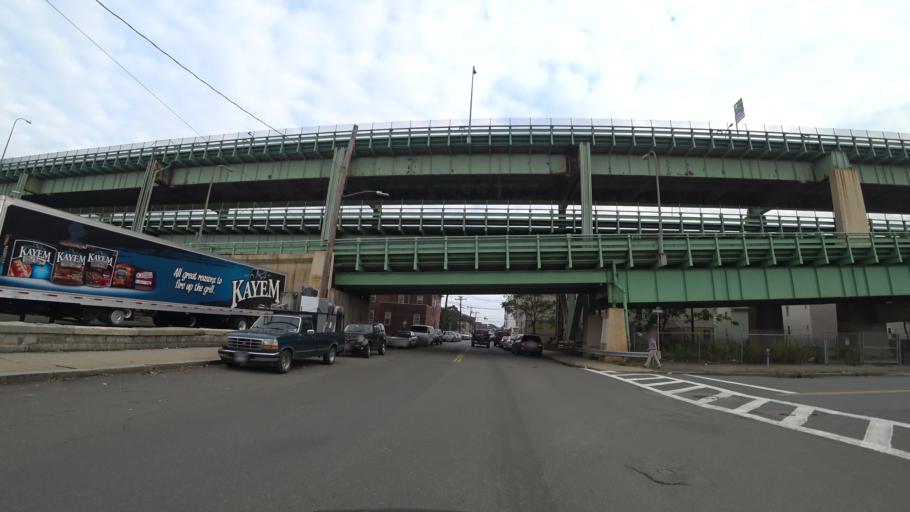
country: US
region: Massachusetts
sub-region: Suffolk County
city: Chelsea
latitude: 42.3912
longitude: -71.0407
